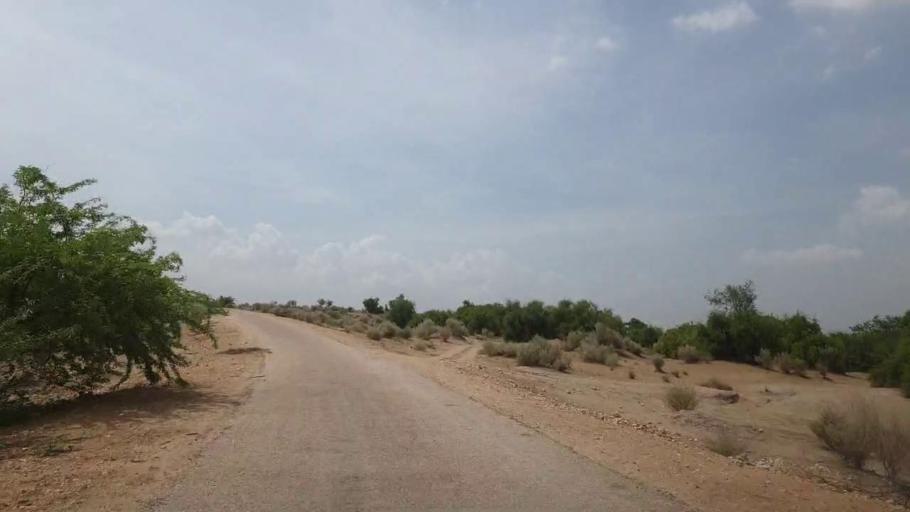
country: PK
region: Sindh
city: Kot Diji
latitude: 27.2354
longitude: 69.0866
